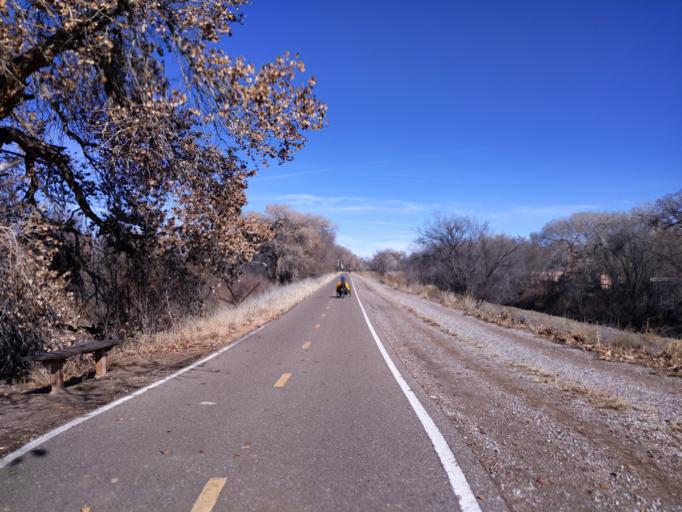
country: US
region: New Mexico
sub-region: Bernalillo County
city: Lee Acres
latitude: 35.1578
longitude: -106.6675
